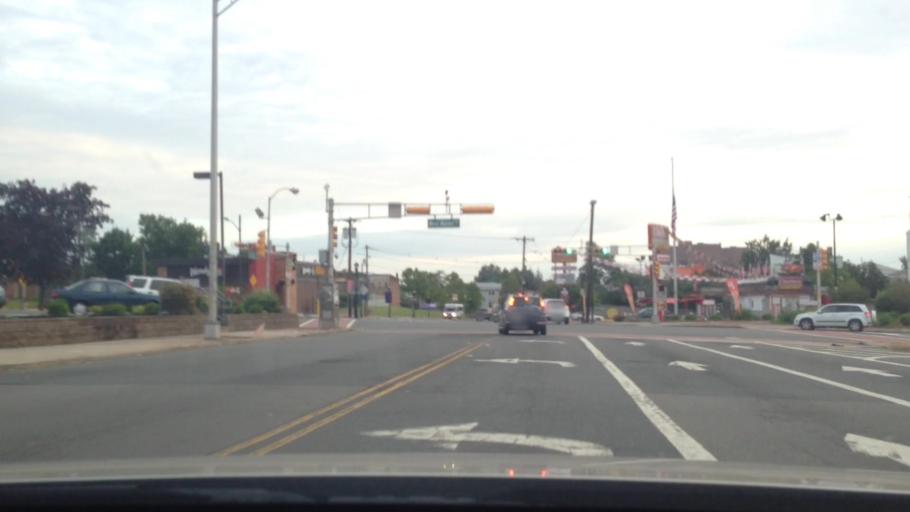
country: US
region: New Jersey
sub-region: Essex County
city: Newark
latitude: 40.7450
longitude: -74.1901
